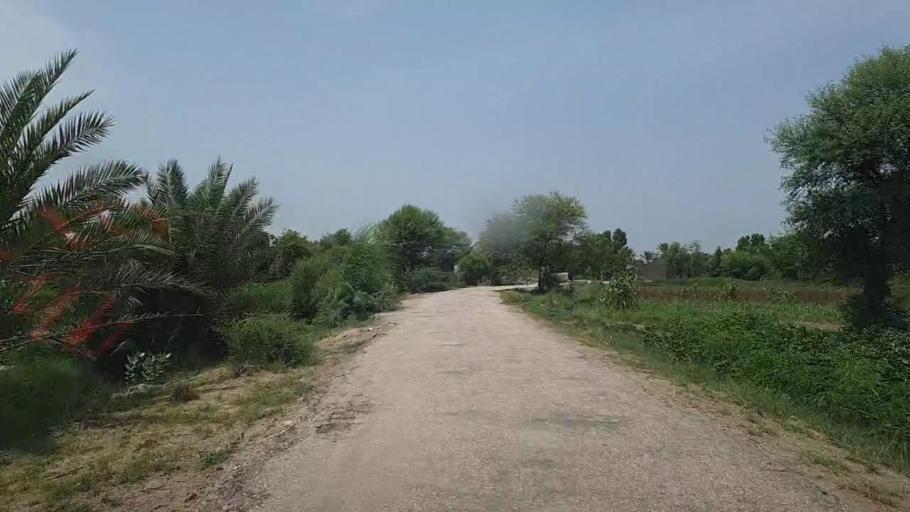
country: PK
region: Sindh
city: Pano Aqil
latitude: 27.8294
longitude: 69.2116
